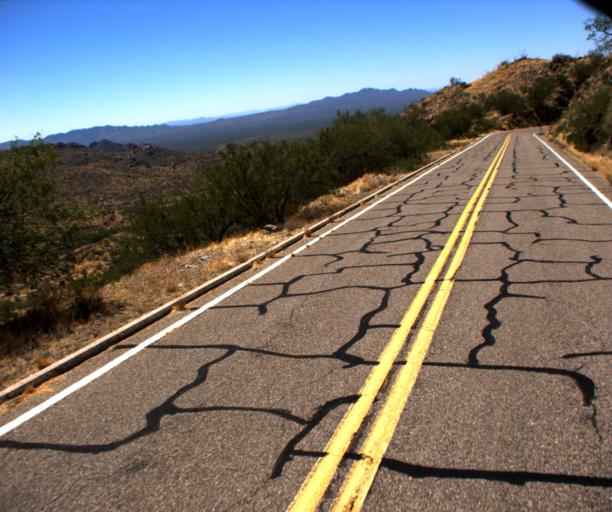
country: US
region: Arizona
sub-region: Pima County
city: Sells
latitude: 31.9838
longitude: -111.6012
